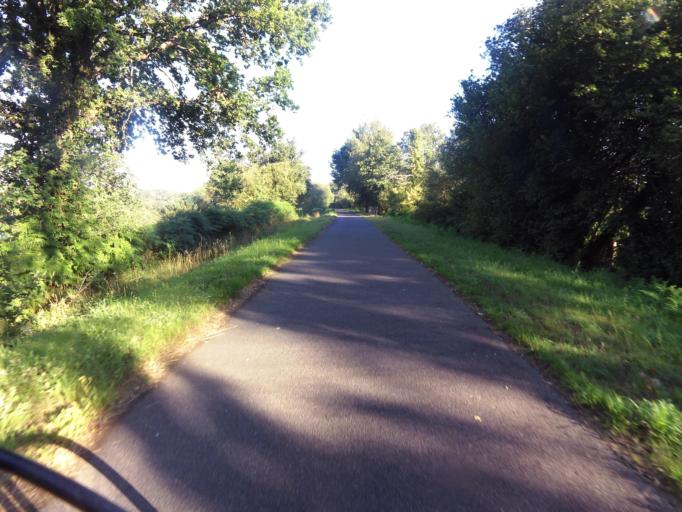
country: FR
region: Brittany
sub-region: Departement du Morbihan
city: Malestroit
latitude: 47.8350
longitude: -2.4232
